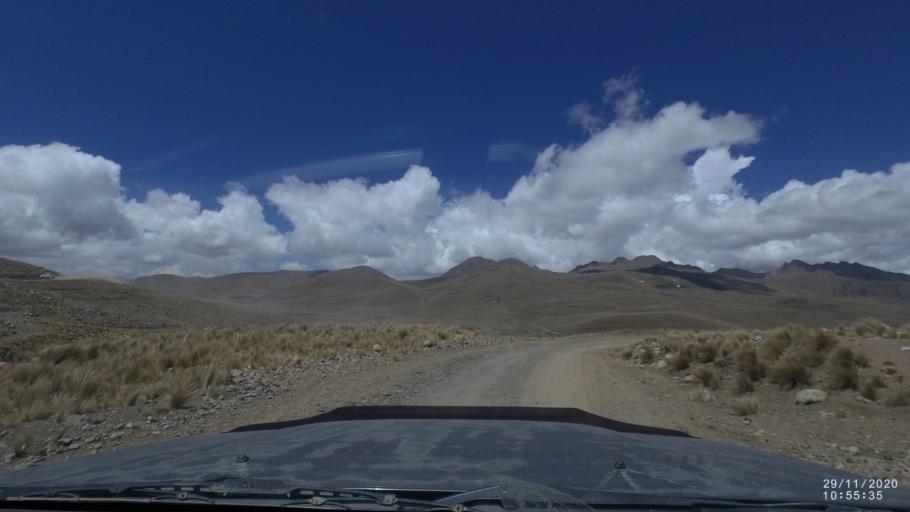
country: BO
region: Cochabamba
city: Cochabamba
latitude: -17.2232
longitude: -66.2219
